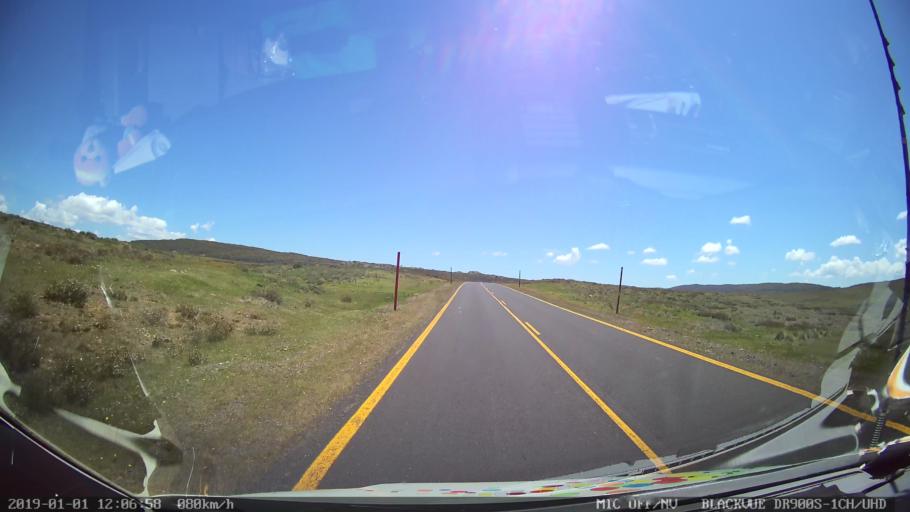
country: AU
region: New South Wales
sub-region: Snowy River
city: Jindabyne
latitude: -35.8385
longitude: 148.4907
